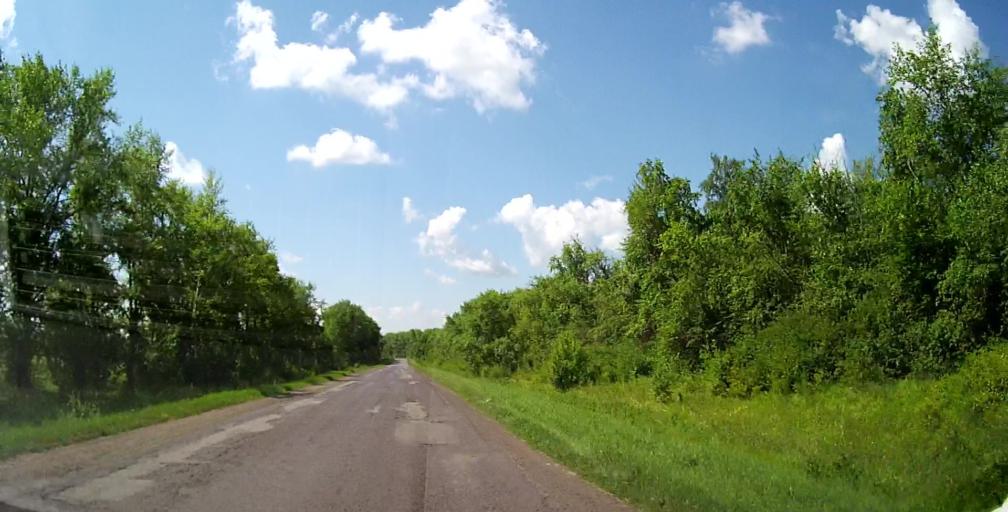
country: RU
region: Lipetsk
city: Chaplygin
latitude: 53.3107
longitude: 39.9560
